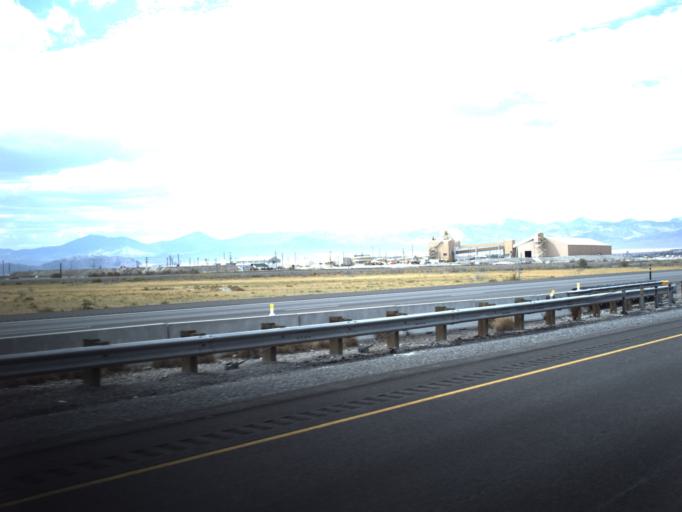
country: US
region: Utah
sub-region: Tooele County
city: Wendover
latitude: 40.7422
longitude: -113.9703
